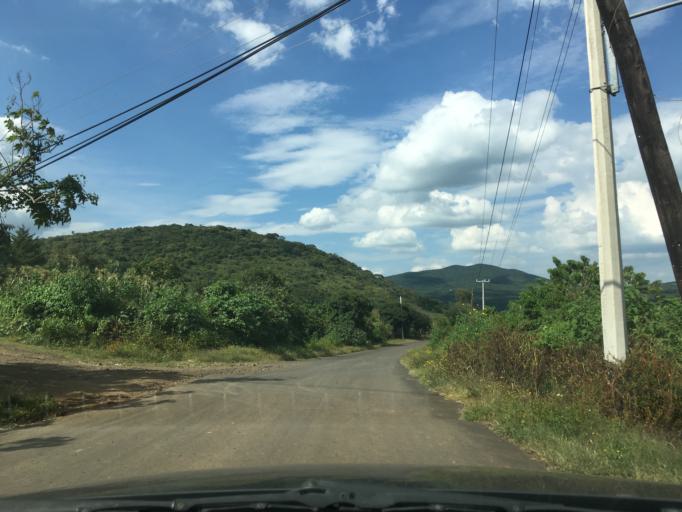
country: MX
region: Mexico
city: El Guayabito
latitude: 19.9012
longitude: -102.4970
